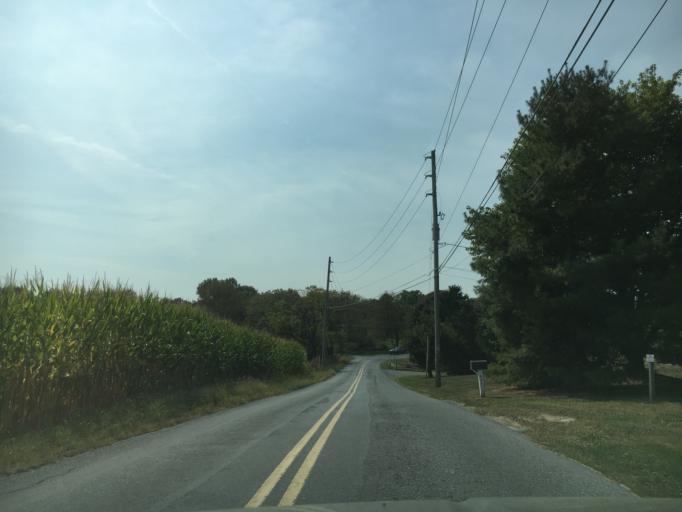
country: US
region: Pennsylvania
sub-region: Berks County
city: Topton
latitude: 40.5530
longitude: -75.7083
